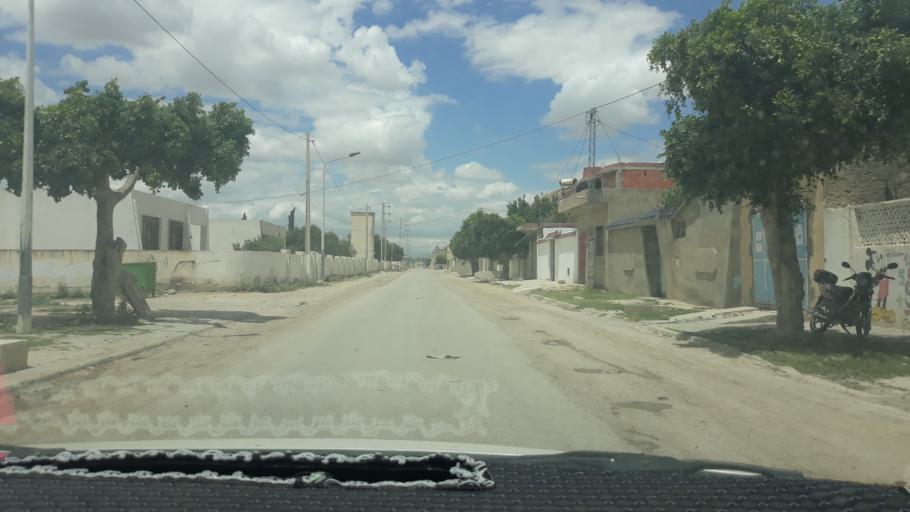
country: TN
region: Al Qayrawan
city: Kairouan
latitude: 35.6182
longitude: 9.9238
